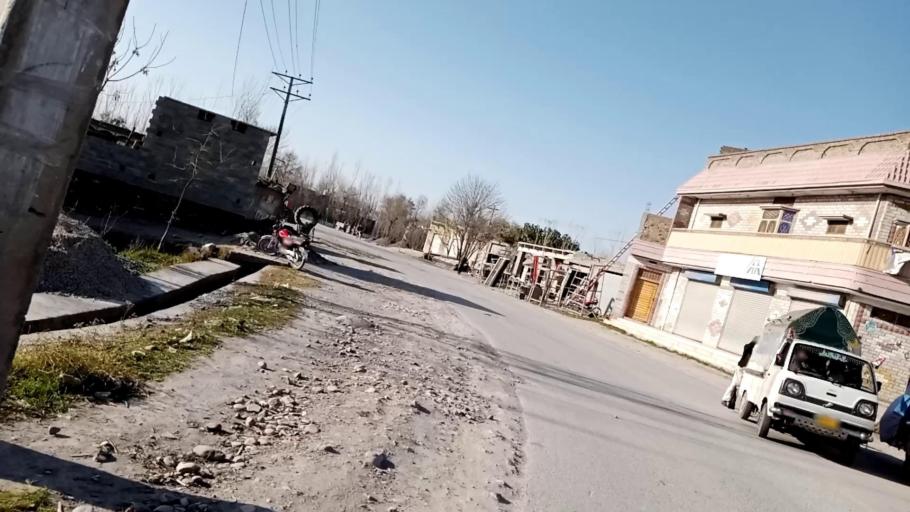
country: PK
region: Khyber Pakhtunkhwa
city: Peshawar
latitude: 34.0700
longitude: 71.5387
